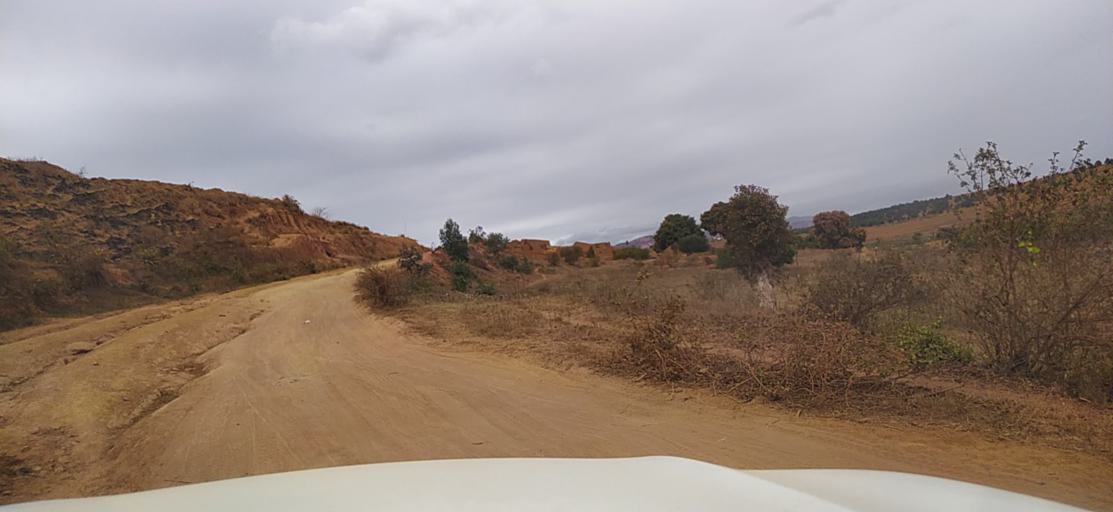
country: MG
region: Alaotra Mangoro
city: Ambatondrazaka
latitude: -17.9120
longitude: 48.2624
